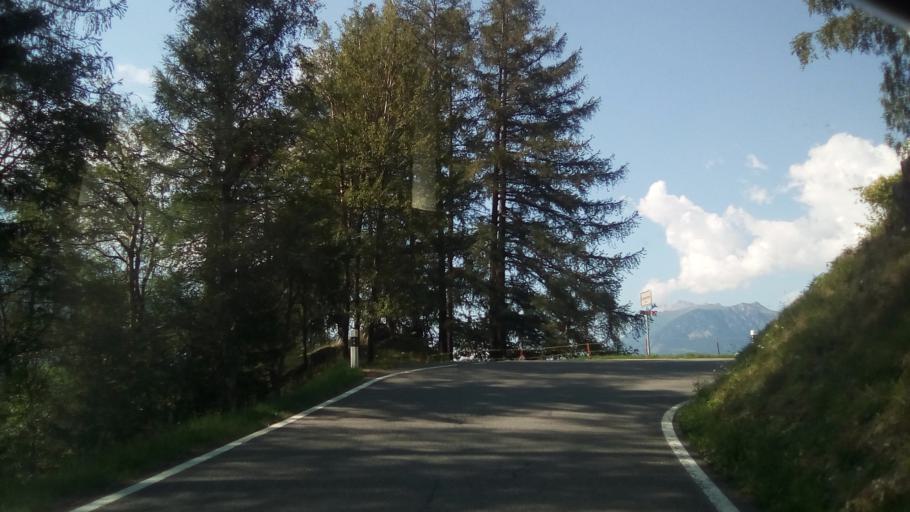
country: CH
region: Valais
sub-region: Martigny District
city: Martigny-Combe
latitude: 46.0648
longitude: 7.0761
